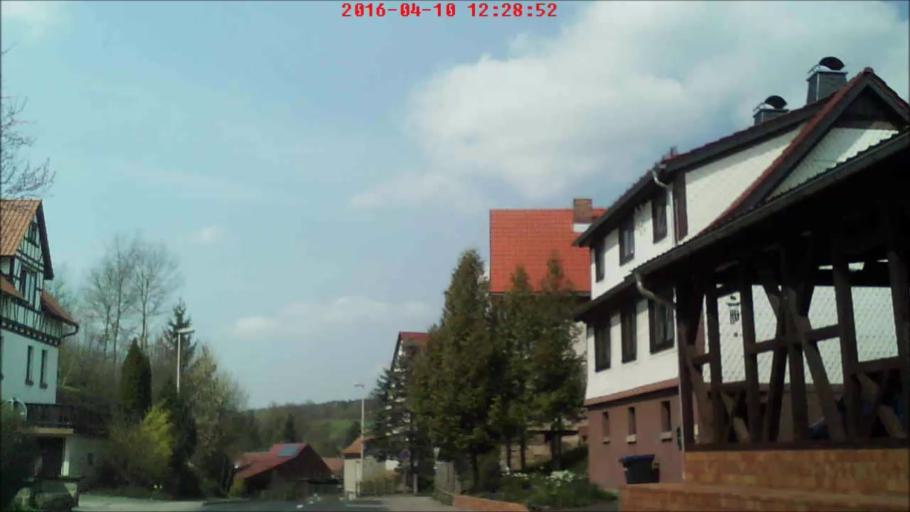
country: DE
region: Thuringia
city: Springstille
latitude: 50.6856
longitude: 10.5286
